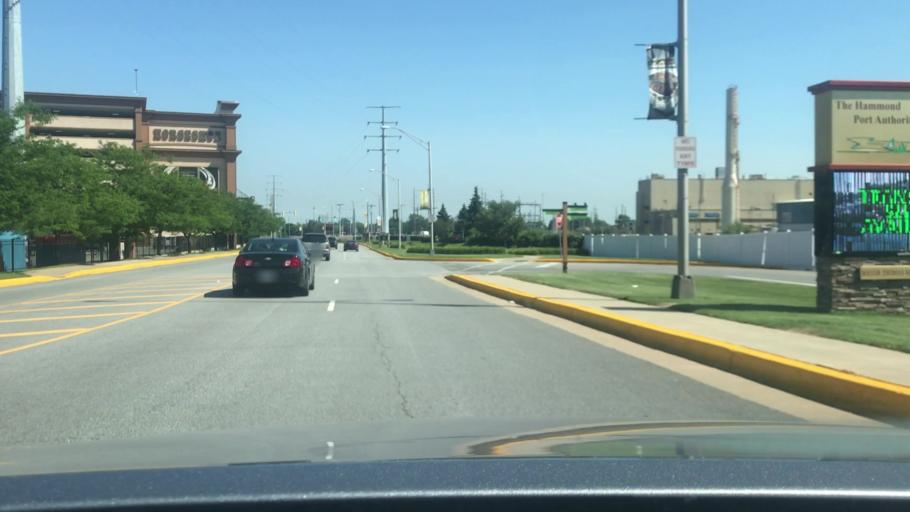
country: US
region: Indiana
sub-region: Lake County
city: Whiting
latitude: 41.6950
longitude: -87.5107
